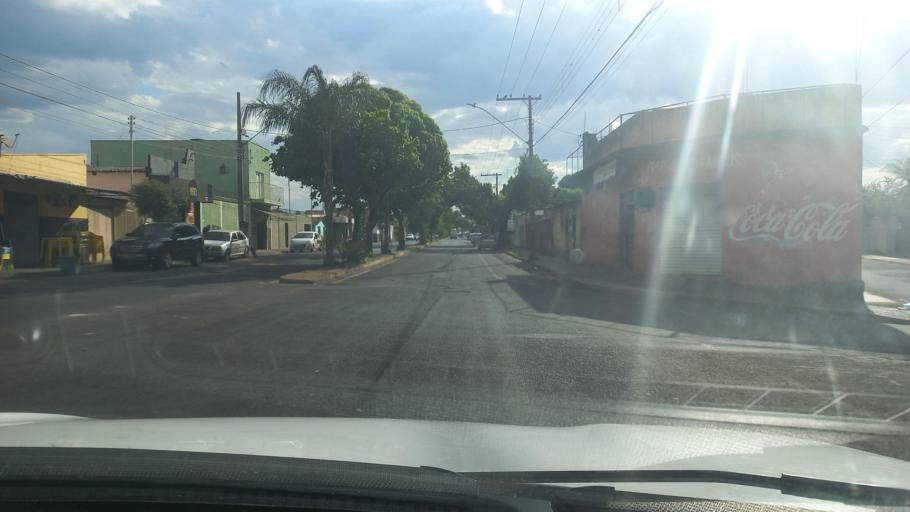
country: BR
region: Minas Gerais
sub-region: Uberaba
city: Uberaba
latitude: -19.7604
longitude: -47.9117
